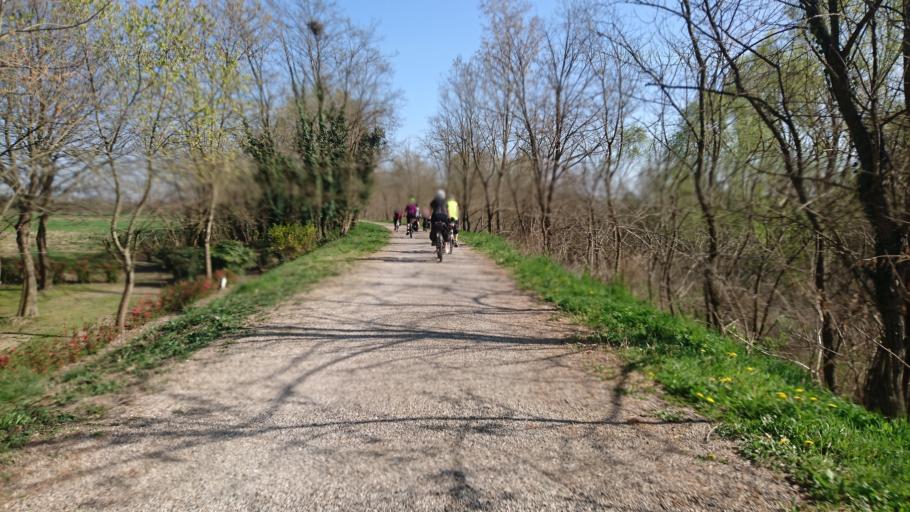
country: IT
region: Veneto
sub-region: Provincia di Padova
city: Limena
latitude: 45.4799
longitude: 11.8491
